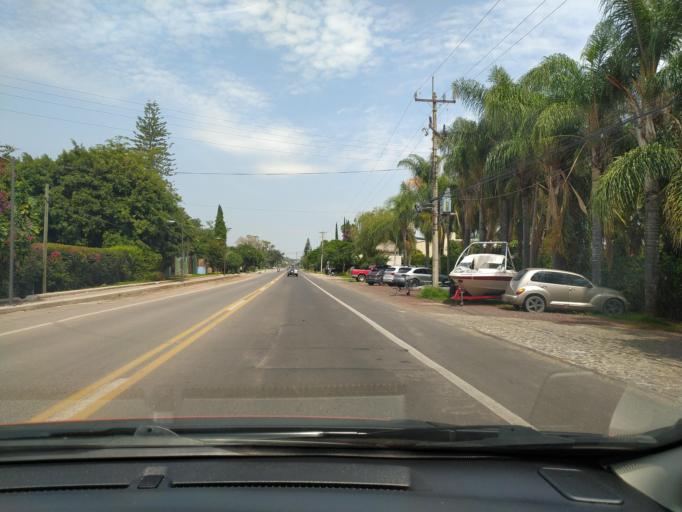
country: MX
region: Jalisco
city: San Juan Cosala
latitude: 20.2902
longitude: -103.3552
